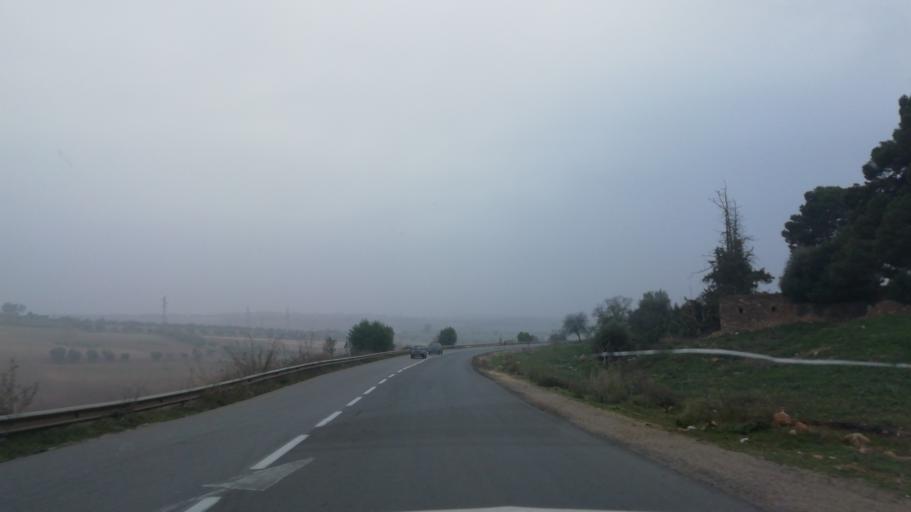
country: DZ
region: Mascara
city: Mascara
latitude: 35.4110
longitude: 0.1590
